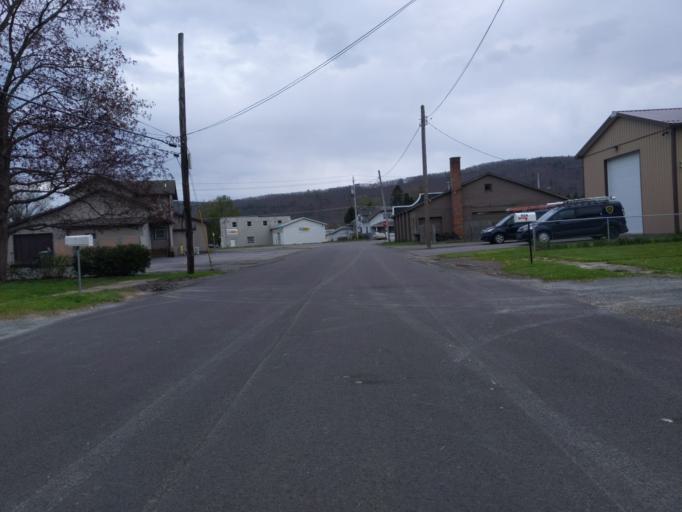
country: US
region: New York
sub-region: Chemung County
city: Southport
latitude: 42.0618
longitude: -76.8104
